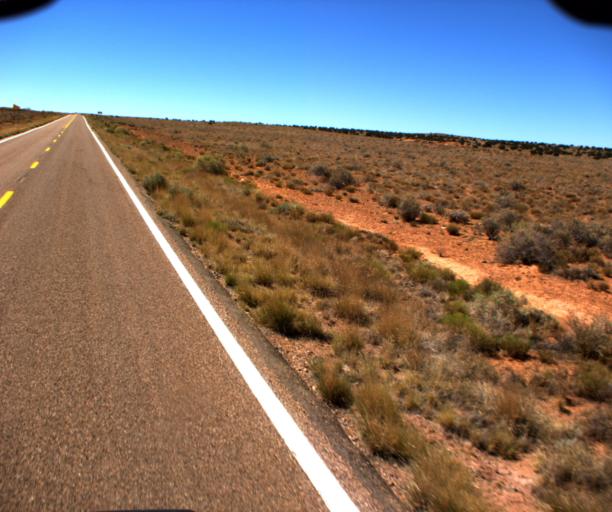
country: US
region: Arizona
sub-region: Navajo County
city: Winslow
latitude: 34.9391
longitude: -110.6427
